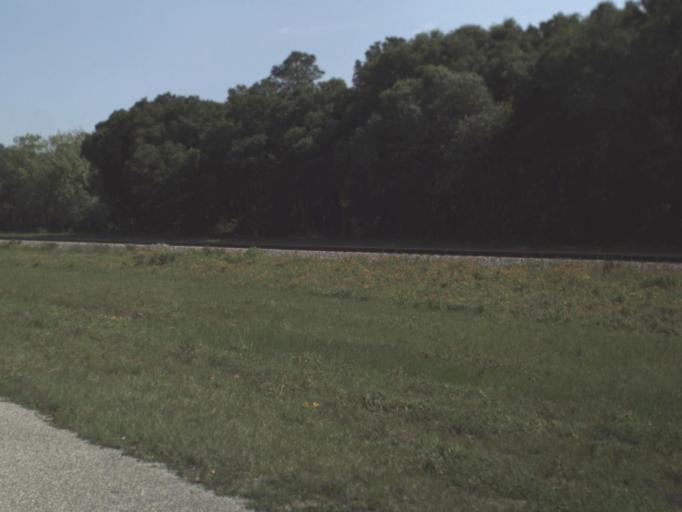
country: US
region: Florida
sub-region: Saint Johns County
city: Villano Beach
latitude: 29.9656
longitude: -81.3506
